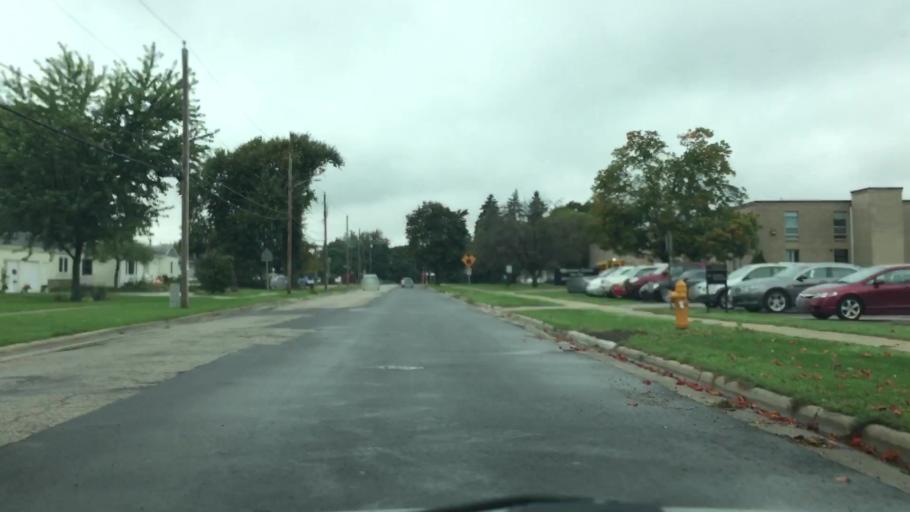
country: US
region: Wisconsin
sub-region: Rock County
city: Janesville
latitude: 42.6643
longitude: -89.0385
